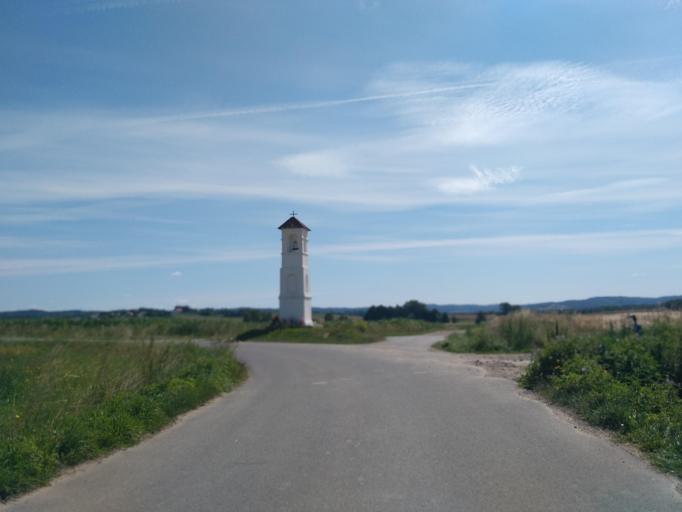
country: PL
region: Subcarpathian Voivodeship
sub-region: Powiat krosnienski
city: Kroscienko Wyzne
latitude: 49.6997
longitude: 21.8298
